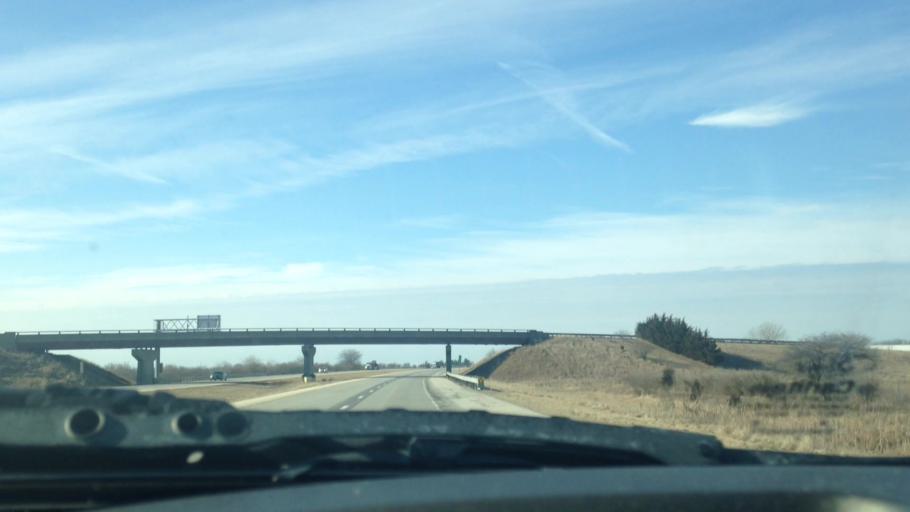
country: US
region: Illinois
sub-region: Ford County
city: Paxton
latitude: 40.5477
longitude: -88.0632
